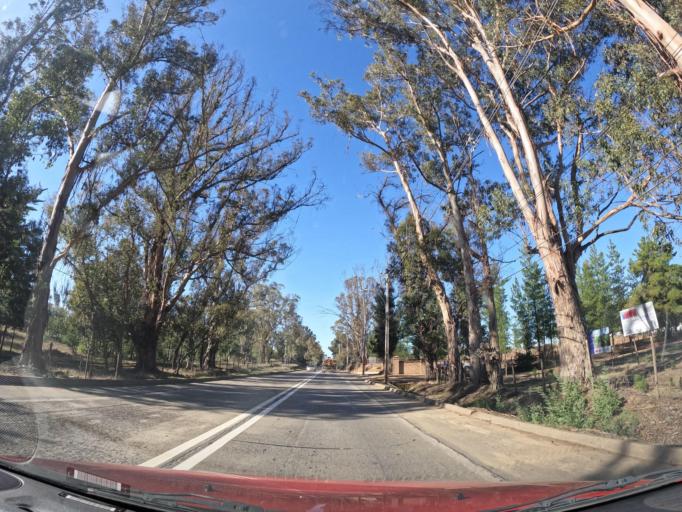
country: CL
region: Maule
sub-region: Provincia de Cauquenes
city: Cauquenes
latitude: -35.9577
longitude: -72.2834
